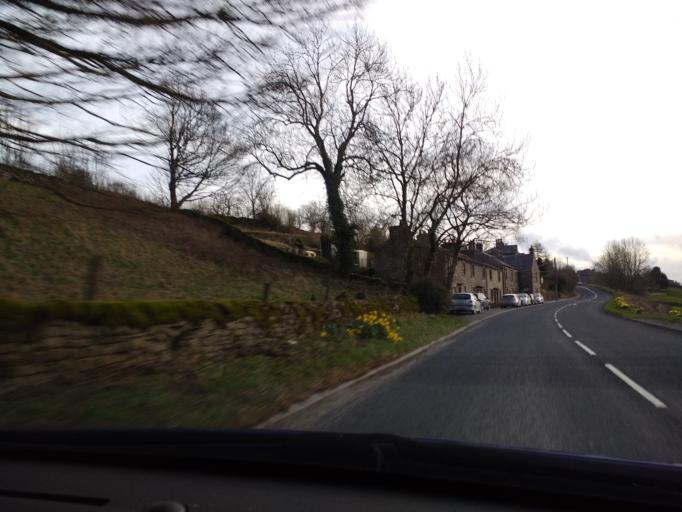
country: GB
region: England
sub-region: North Yorkshire
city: Settle
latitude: 54.0883
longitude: -2.2732
